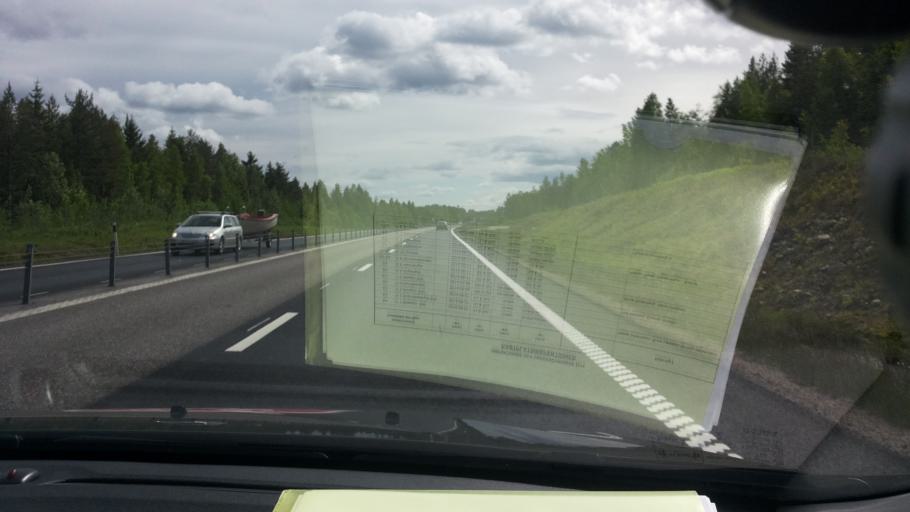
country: SE
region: Vaesternorrland
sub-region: Sundsvalls Kommun
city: Njurundabommen
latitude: 62.1776
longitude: 17.3575
